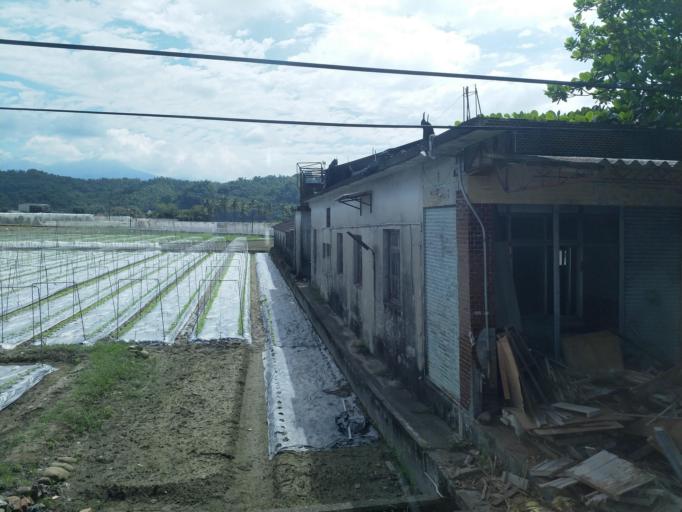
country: TW
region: Taiwan
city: Yujing
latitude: 22.9082
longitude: 120.5596
